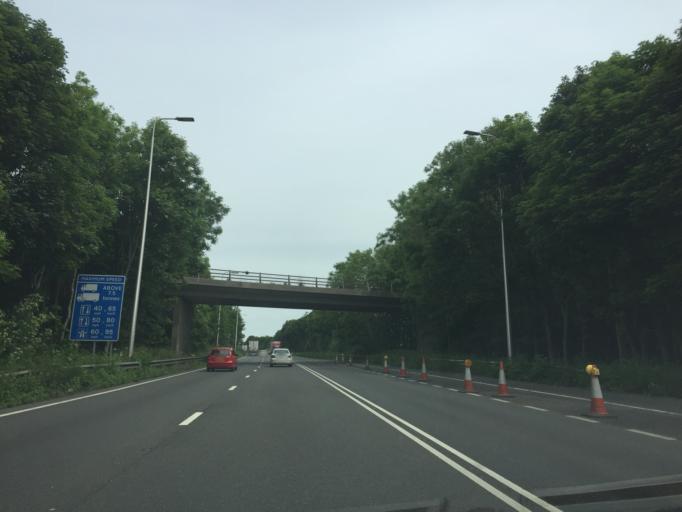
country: GB
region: England
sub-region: Kent
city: Dover
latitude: 51.1328
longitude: 1.3295
